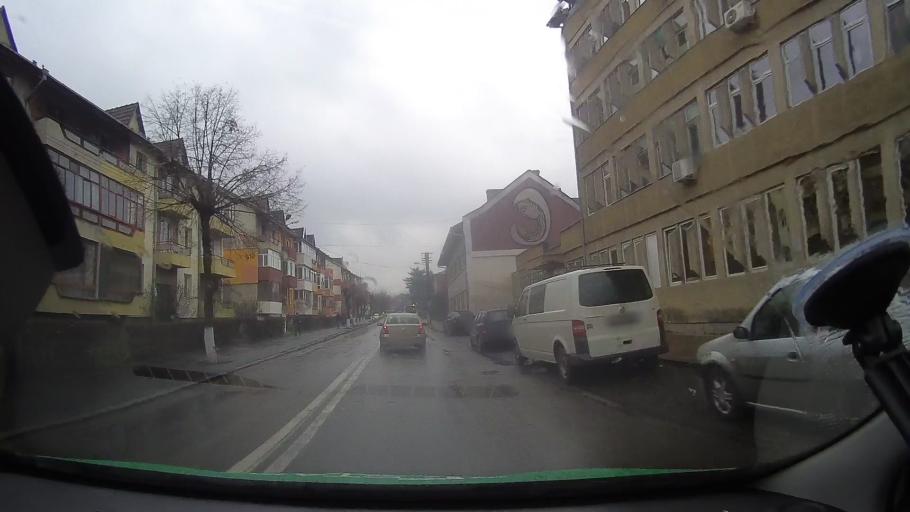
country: RO
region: Hunedoara
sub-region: Municipiul Brad
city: Brad
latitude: 46.1264
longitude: 22.7916
